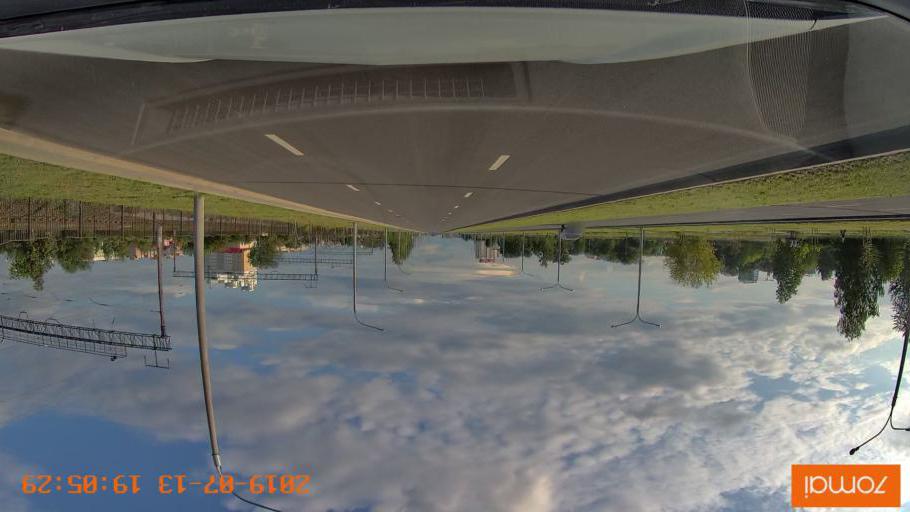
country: BY
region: Minsk
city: Syenitsa
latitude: 53.8616
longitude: 27.5589
